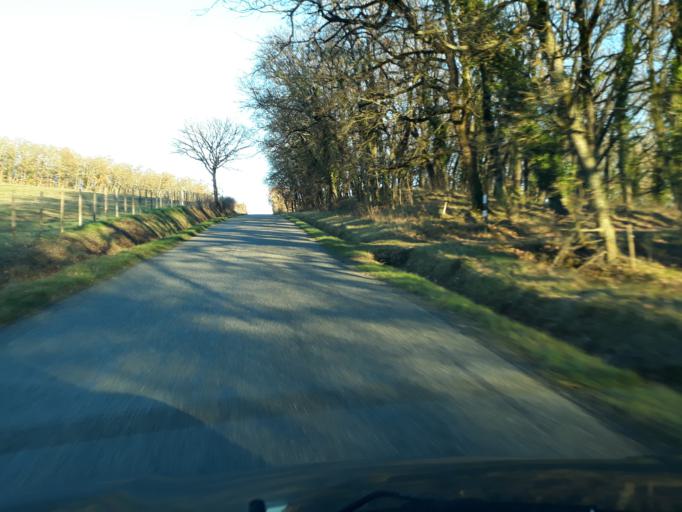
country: FR
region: Midi-Pyrenees
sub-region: Departement du Gers
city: Gimont
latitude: 43.6242
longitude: 0.9110
